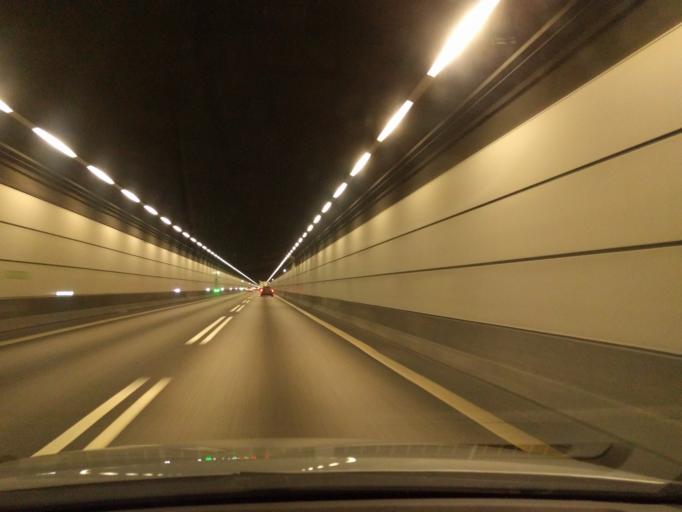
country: DK
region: Capital Region
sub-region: Dragor Kommune
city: Dragor
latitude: 55.6146
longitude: 12.7187
